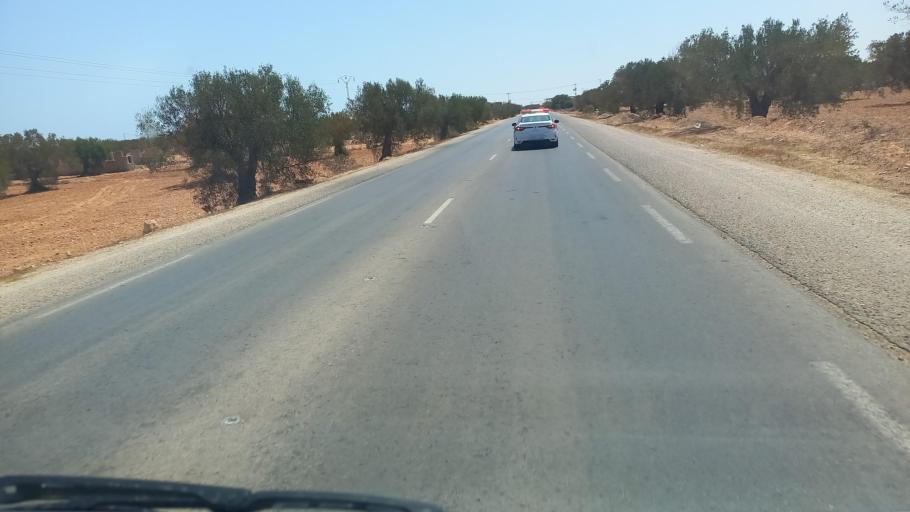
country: TN
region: Madanin
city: Zarzis
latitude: 33.5523
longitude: 11.0646
